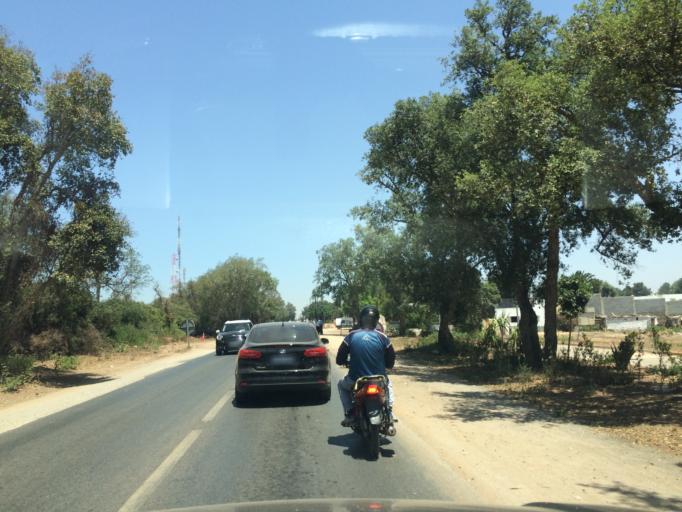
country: MA
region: Rabat-Sale-Zemmour-Zaer
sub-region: Skhirate-Temara
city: Temara
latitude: 33.9089
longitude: -6.8192
